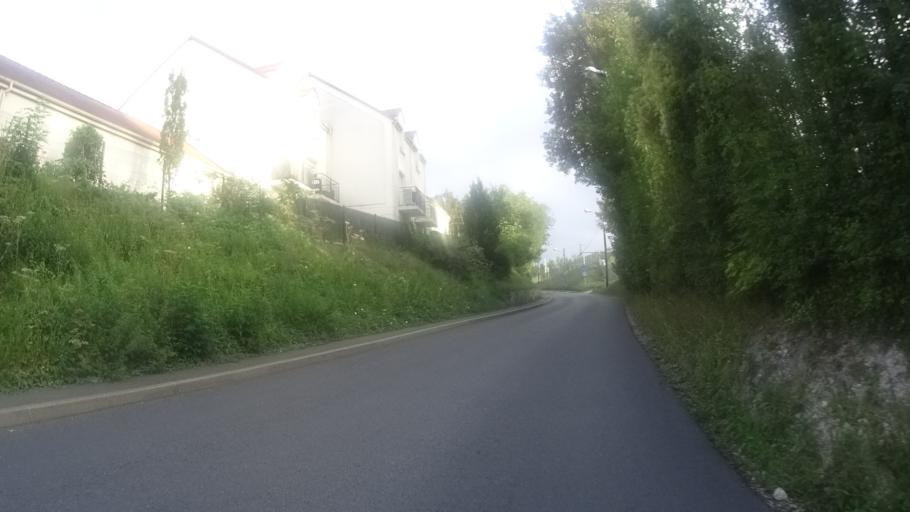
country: FR
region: Ile-de-France
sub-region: Departement de l'Essonne
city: Villabe
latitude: 48.5880
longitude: 2.4664
